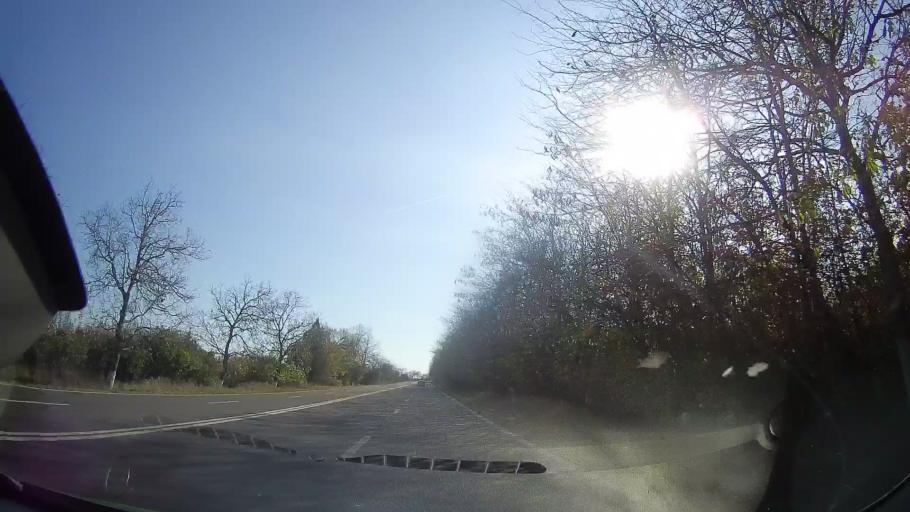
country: RO
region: Constanta
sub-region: Comuna Douazeci si Trei August
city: Douazeci si Trei August
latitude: 43.8901
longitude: 28.5725
